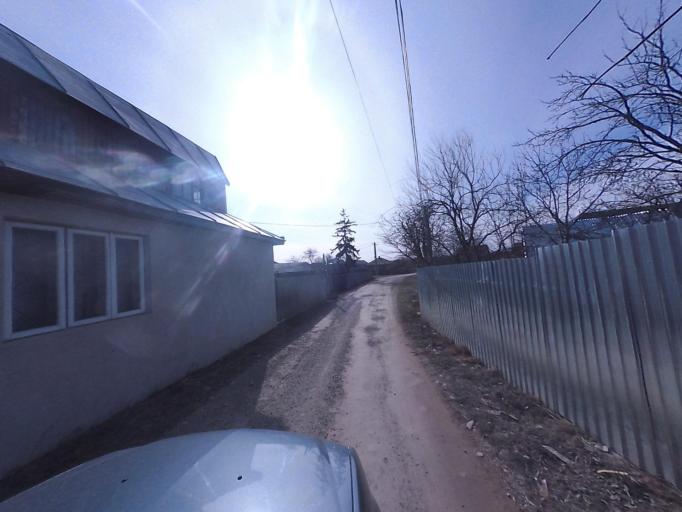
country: RO
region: Neamt
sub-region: Oras Targu Neamt
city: Humulesti
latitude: 47.2131
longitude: 26.3355
